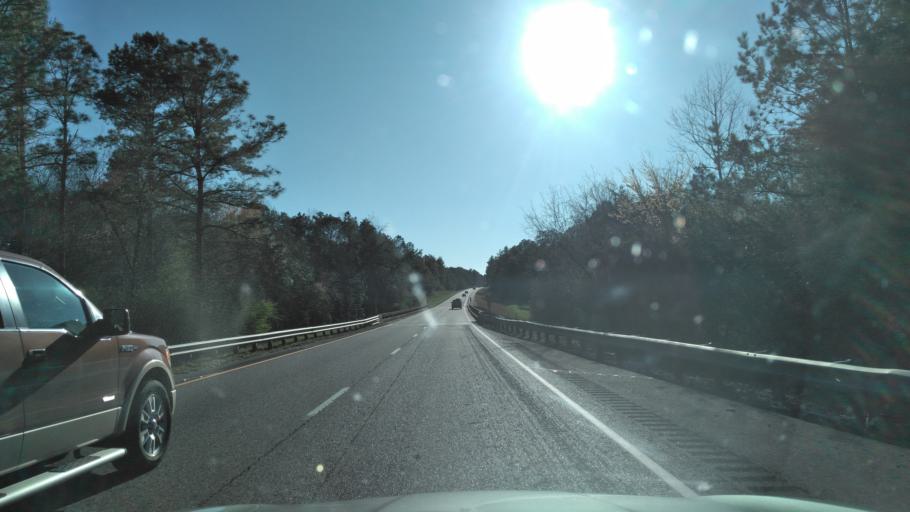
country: US
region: Alabama
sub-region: Escambia County
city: Atmore
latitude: 31.0484
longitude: -87.5977
